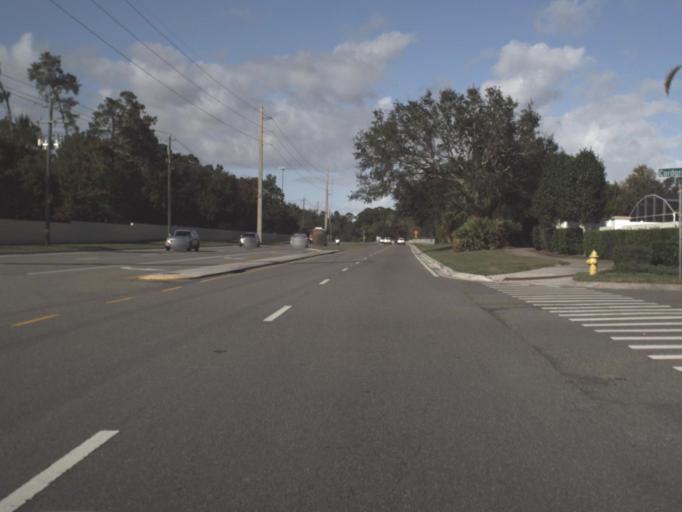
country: US
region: Florida
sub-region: Volusia County
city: Port Orange
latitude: 29.0964
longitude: -81.0288
